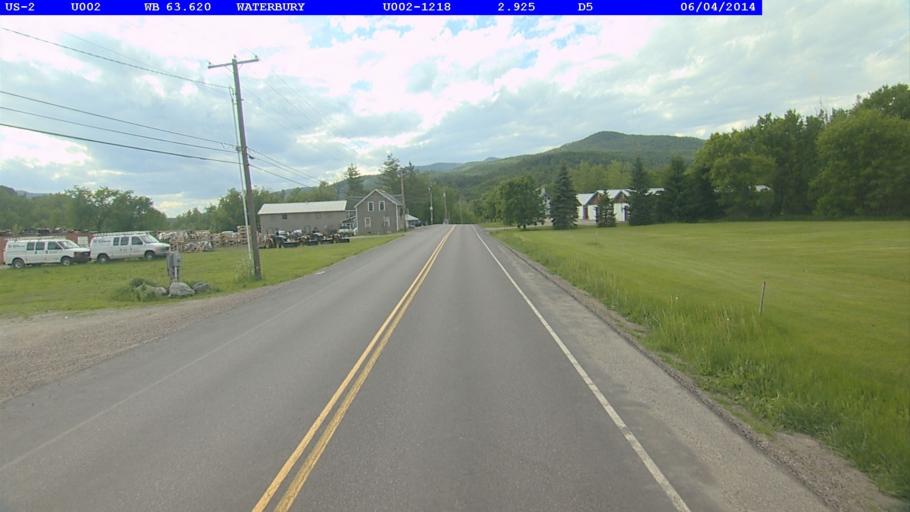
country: US
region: Vermont
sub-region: Washington County
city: Waterbury
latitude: 44.3489
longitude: -72.7728
